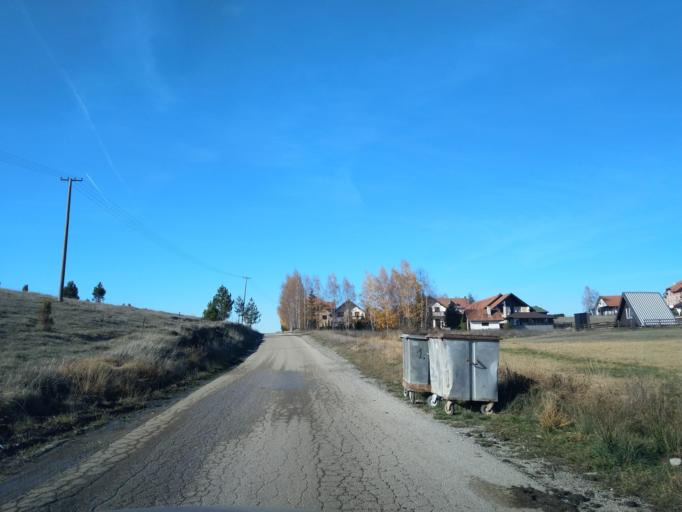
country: RS
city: Zlatibor
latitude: 43.7378
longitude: 19.6774
